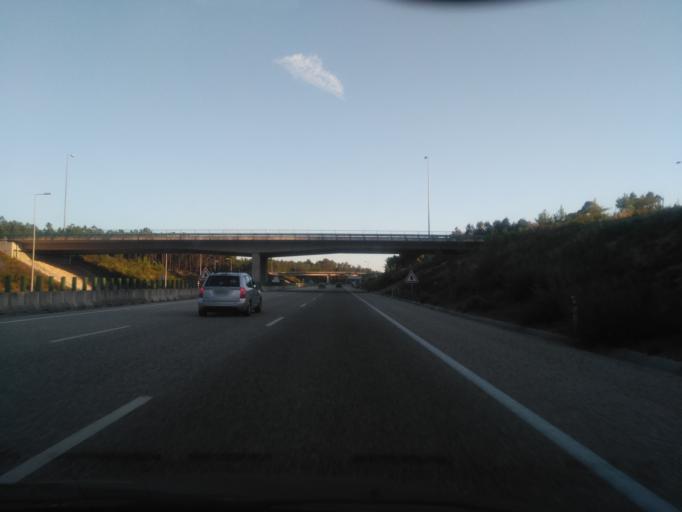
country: PT
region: Leiria
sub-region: Pombal
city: Lourical
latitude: 39.9451
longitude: -8.7706
